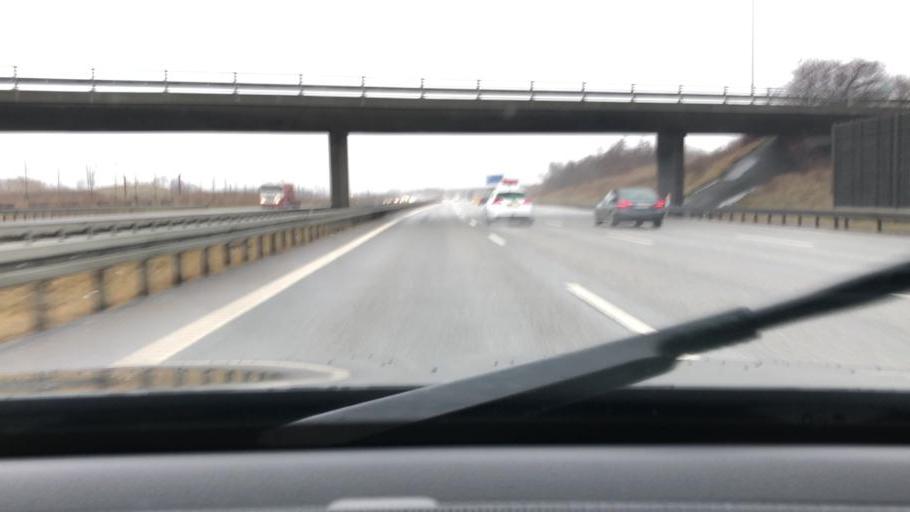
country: DK
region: Zealand
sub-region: Solrod Kommune
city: Solrod Strand
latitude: 55.5679
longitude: 12.2403
